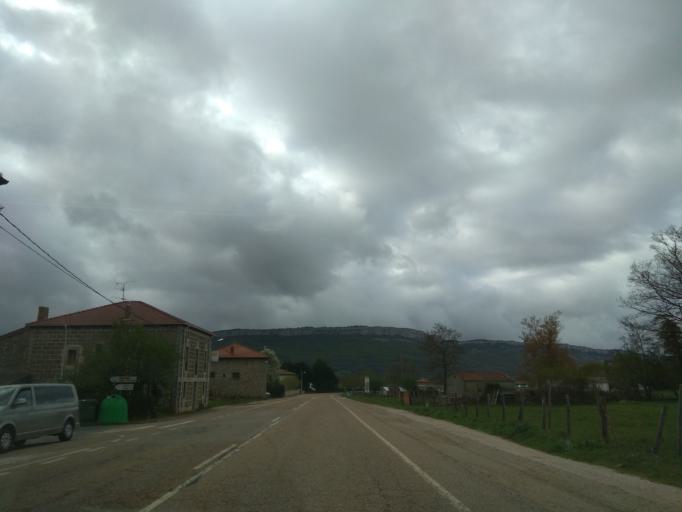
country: ES
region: Castille and Leon
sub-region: Provincia de Burgos
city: Espinosa de los Monteros
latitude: 43.0994
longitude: -3.4537
